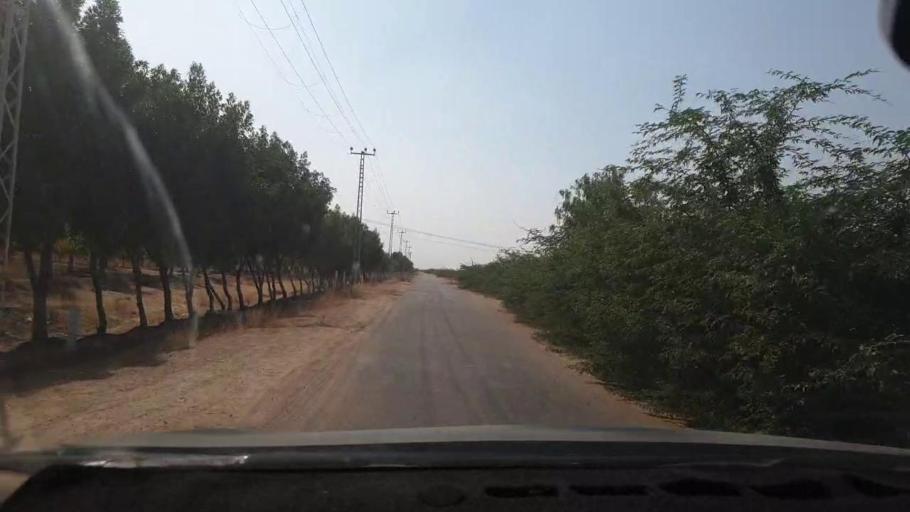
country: PK
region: Sindh
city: Malir Cantonment
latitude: 25.1127
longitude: 67.2069
